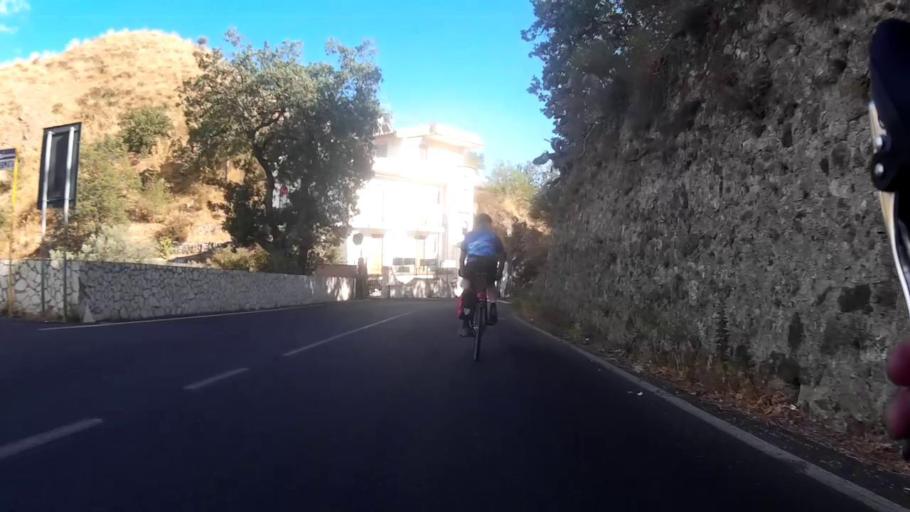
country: IT
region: Sicily
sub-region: Messina
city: Castelmola
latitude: 37.8609
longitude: 15.2800
